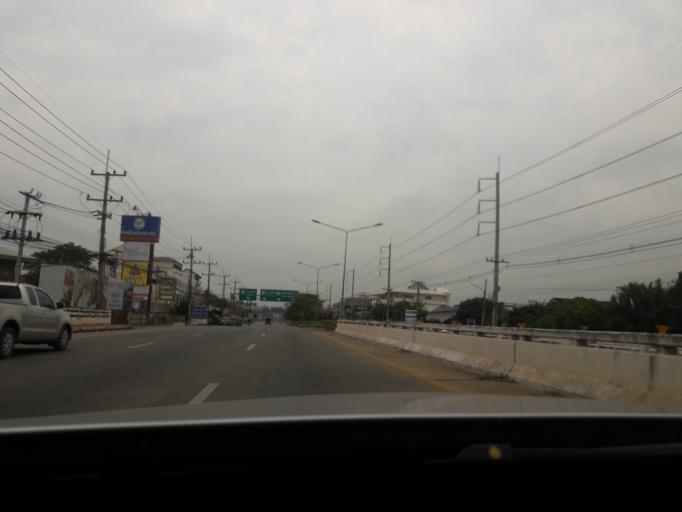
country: TH
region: Samut Songkhram
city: Samut Songkhram
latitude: 13.4214
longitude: 99.9889
